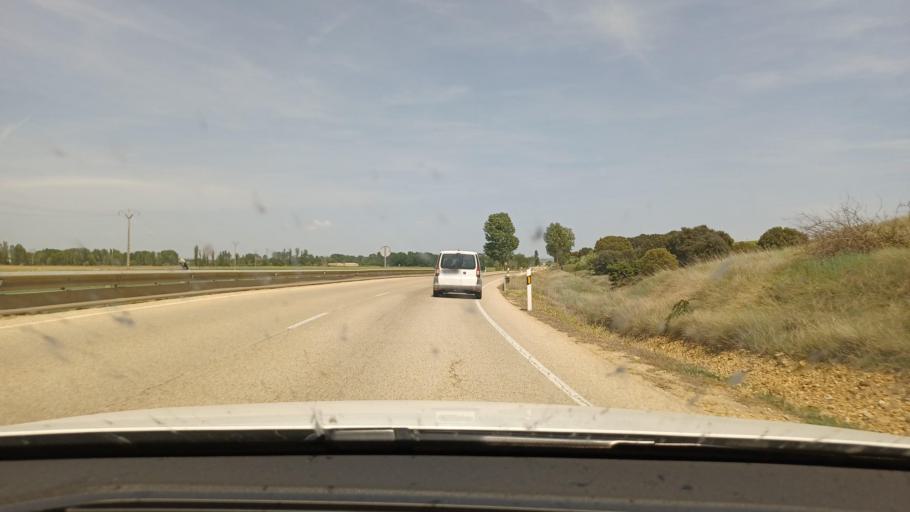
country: ES
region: Castille and Leon
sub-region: Provincia de Soria
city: Almazan
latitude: 41.4714
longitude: -2.5760
